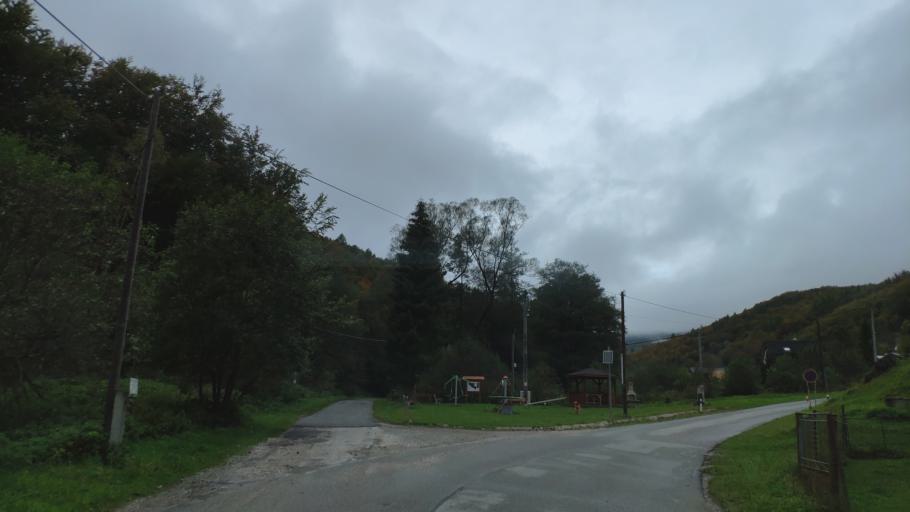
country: SK
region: Kosicky
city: Medzev
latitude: 48.7467
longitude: 21.0037
